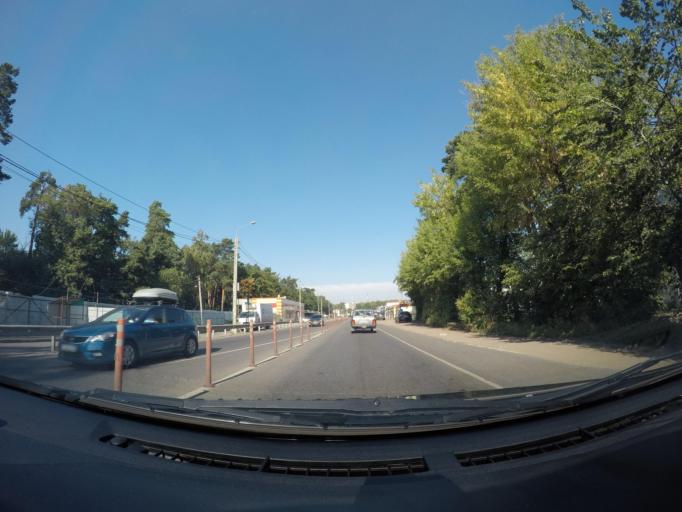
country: RU
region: Moskovskaya
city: Malakhovka
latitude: 55.6603
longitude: 38.0207
